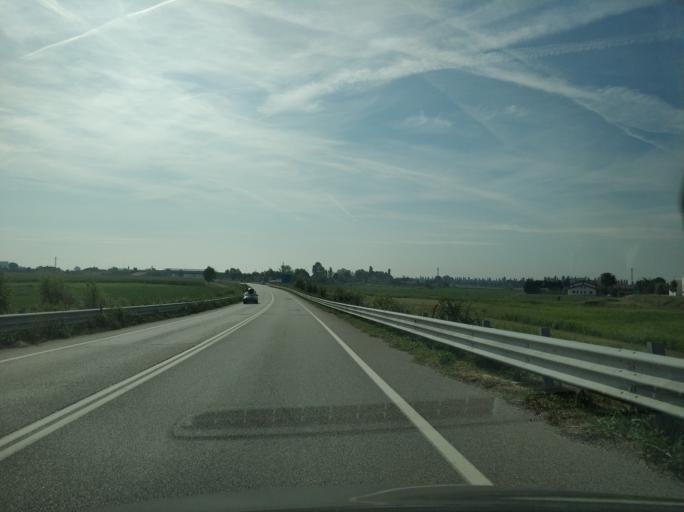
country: IT
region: Veneto
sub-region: Provincia di Padova
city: Sant'Elena
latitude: 45.2090
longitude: 11.7242
